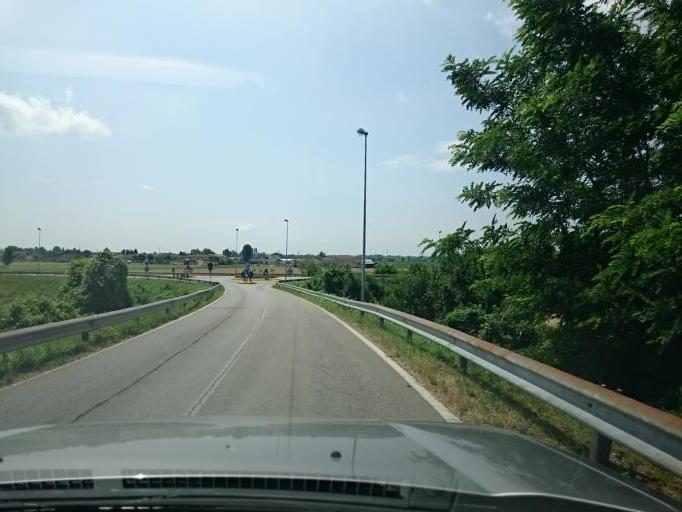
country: IT
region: Veneto
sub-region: Provincia di Padova
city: Masera di Padova
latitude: 45.3384
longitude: 11.8525
